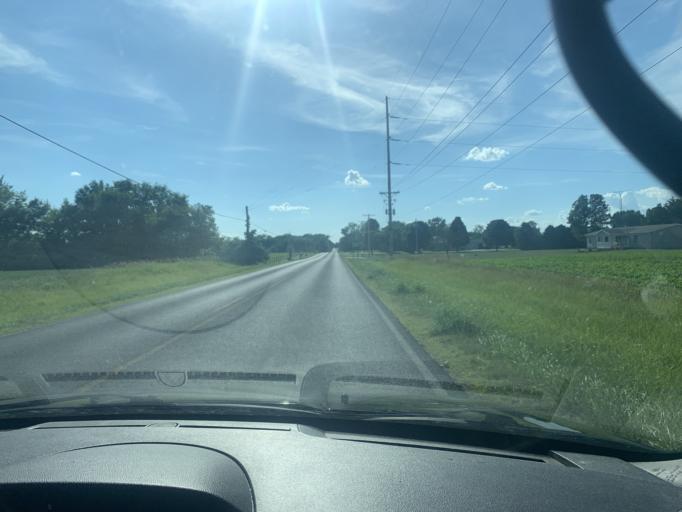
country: US
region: Ohio
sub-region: Logan County
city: Bellefontaine
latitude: 40.3480
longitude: -83.7832
